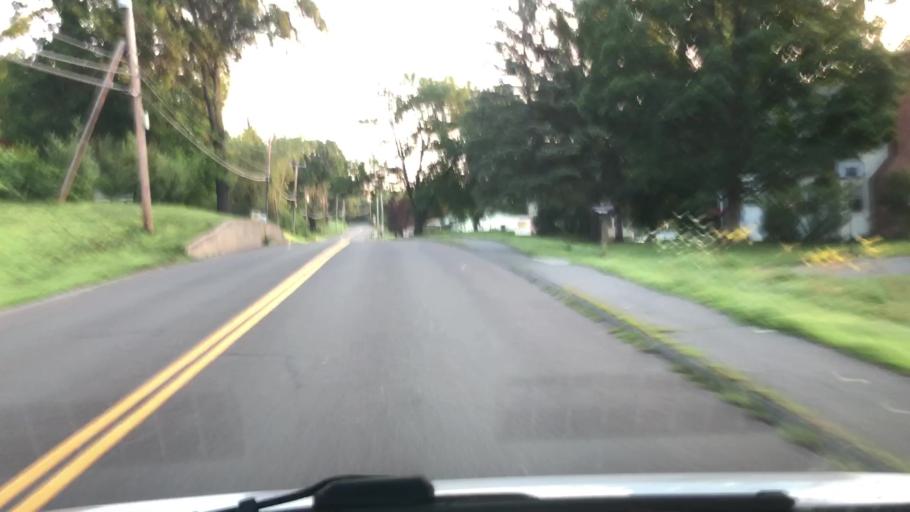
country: US
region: Massachusetts
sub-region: Hampshire County
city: Easthampton
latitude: 42.2430
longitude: -72.6831
